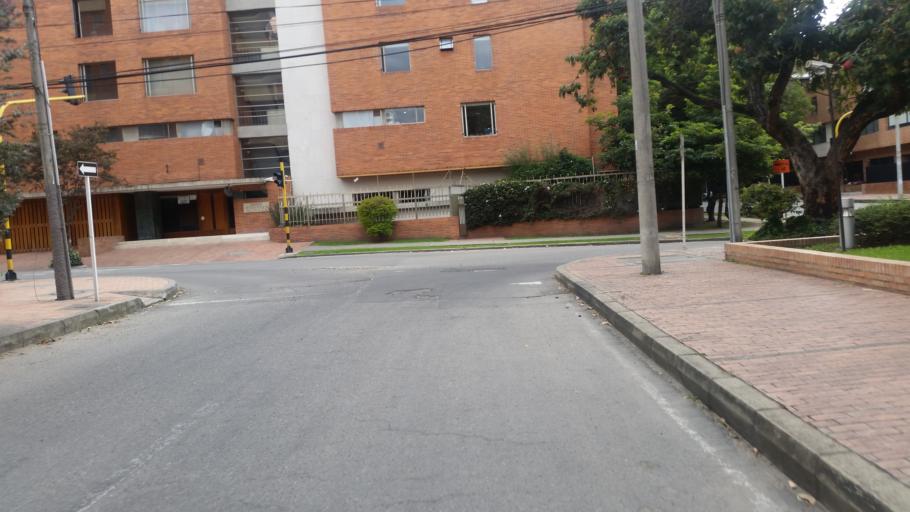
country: CO
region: Bogota D.C.
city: Barrio San Luis
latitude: 4.6775
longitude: -74.0426
